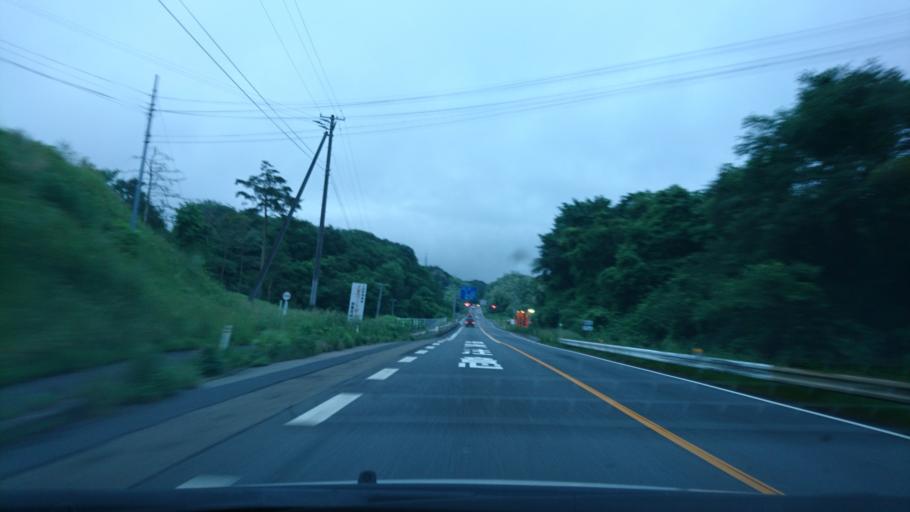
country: JP
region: Iwate
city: Ichinoseki
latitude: 38.8796
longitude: 141.1182
